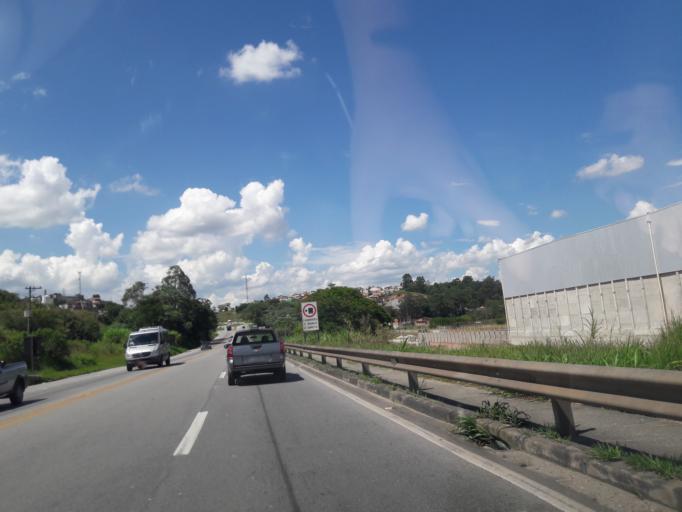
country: BR
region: Sao Paulo
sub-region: Cajamar
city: Cajamar
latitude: -23.3423
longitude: -46.8310
